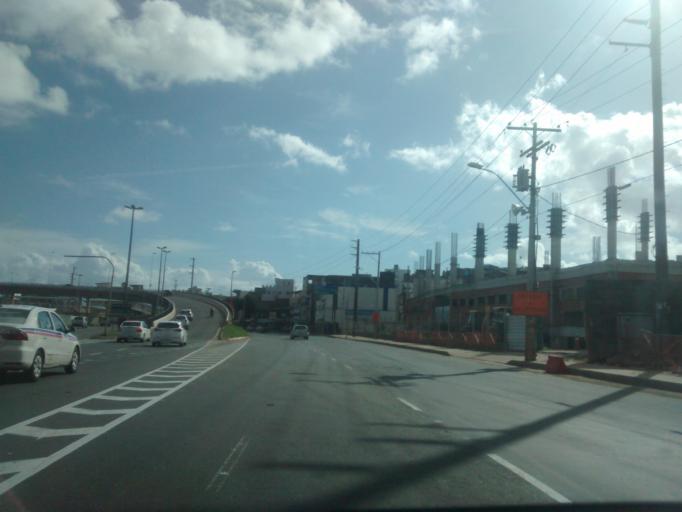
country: BR
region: Bahia
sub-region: Salvador
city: Salvador
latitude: -12.9753
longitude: -38.4579
